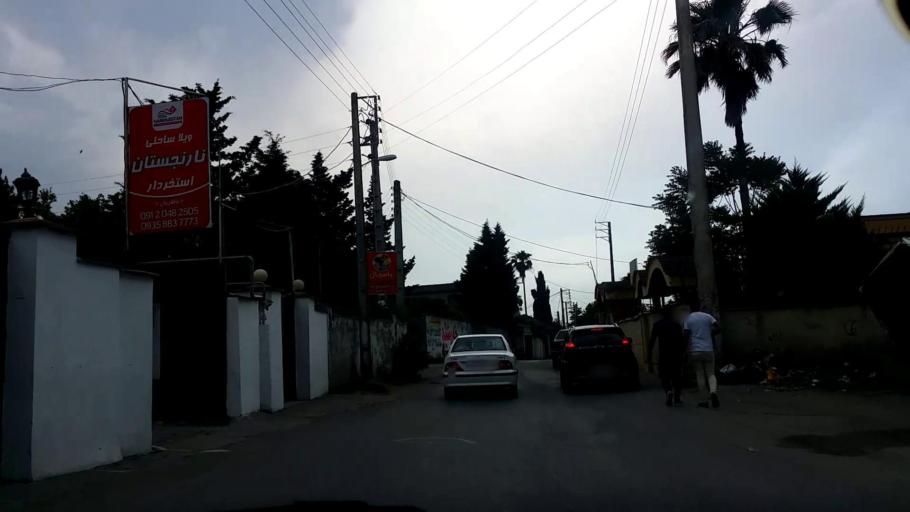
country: IR
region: Mazandaran
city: Chalus
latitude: 36.6862
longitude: 51.4103
